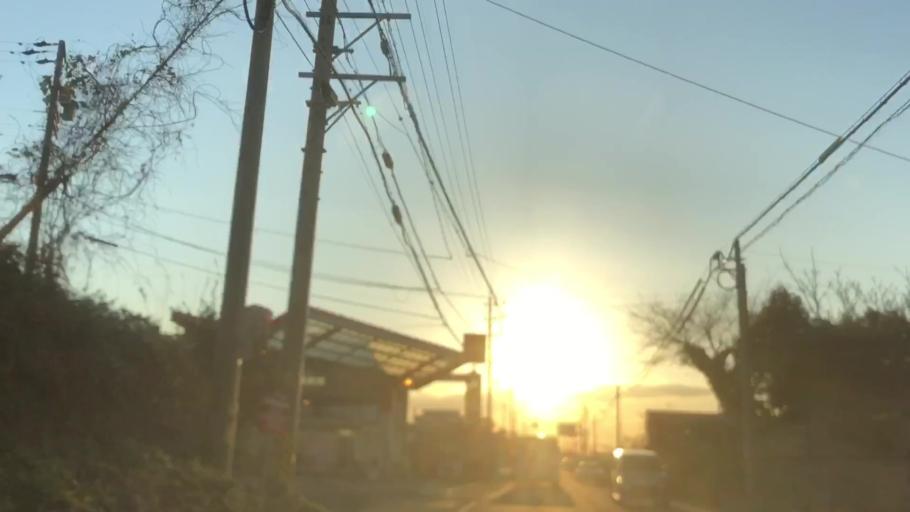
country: JP
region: Aichi
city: Tahara
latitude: 34.6378
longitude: 137.1316
